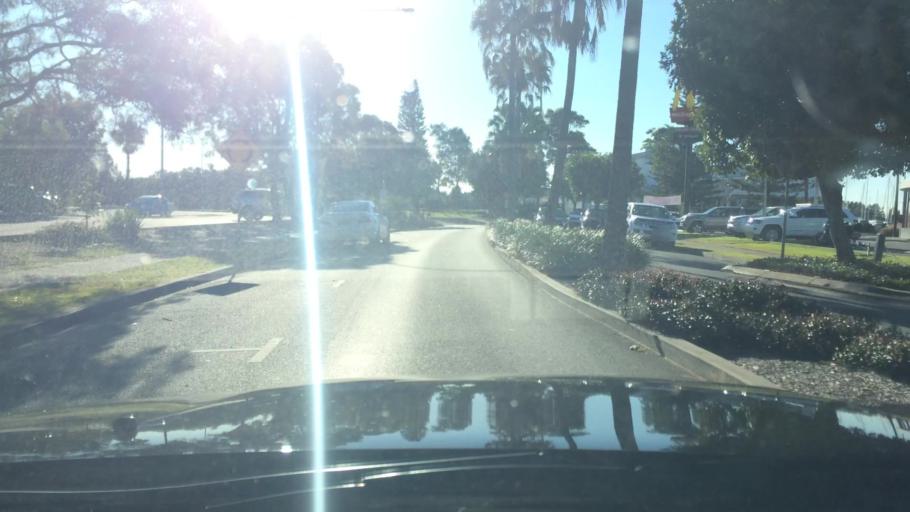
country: AU
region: New South Wales
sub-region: Port Macquarie-Hastings
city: Port Macquarie
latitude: -31.4278
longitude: 152.8962
